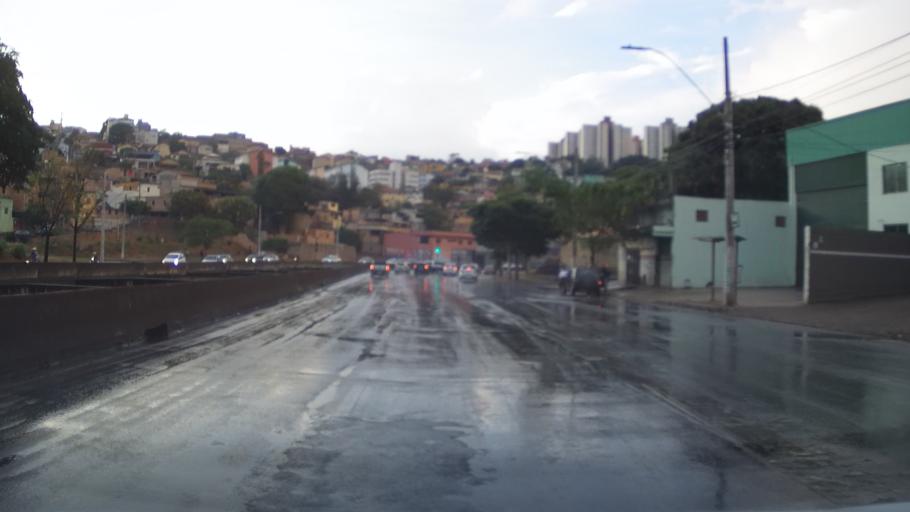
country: BR
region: Minas Gerais
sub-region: Belo Horizonte
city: Belo Horizonte
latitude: -19.9439
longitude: -43.9872
